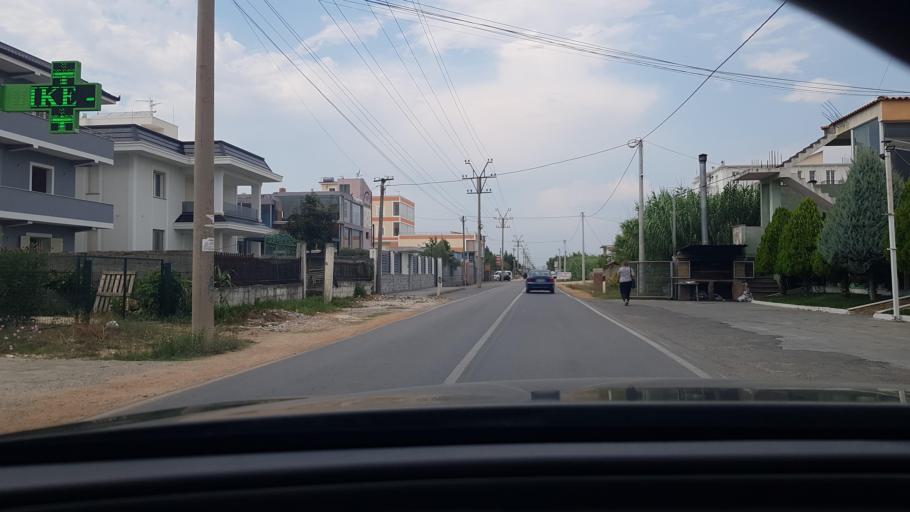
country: AL
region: Durres
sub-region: Rrethi i Durresit
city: Sukth
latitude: 41.3977
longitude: 19.5466
